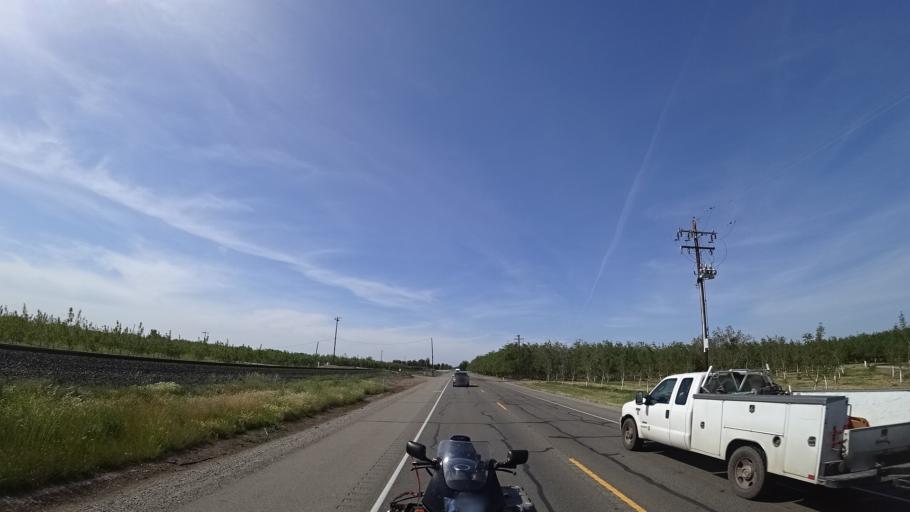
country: US
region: California
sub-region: Tehama County
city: Los Molinos
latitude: 40.0028
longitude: -122.0907
